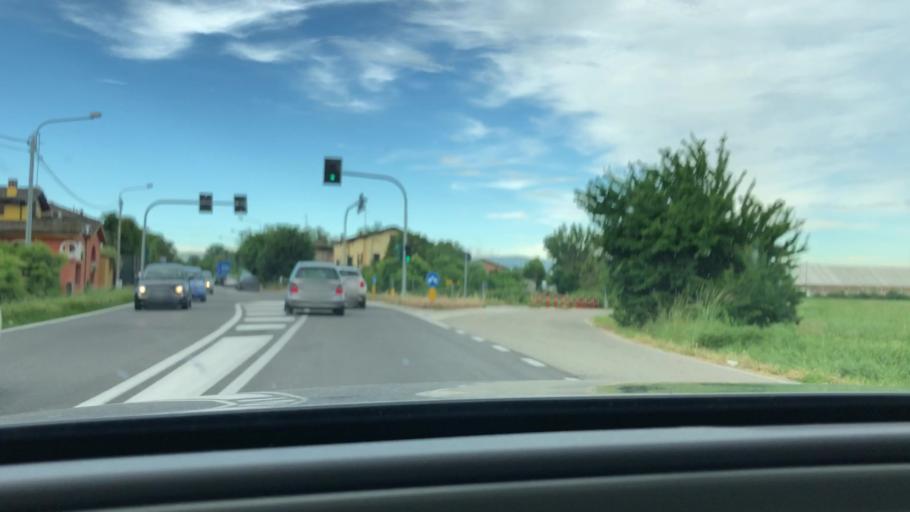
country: IT
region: Emilia-Romagna
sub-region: Provincia di Modena
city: San Damaso
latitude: 44.6043
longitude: 10.9323
